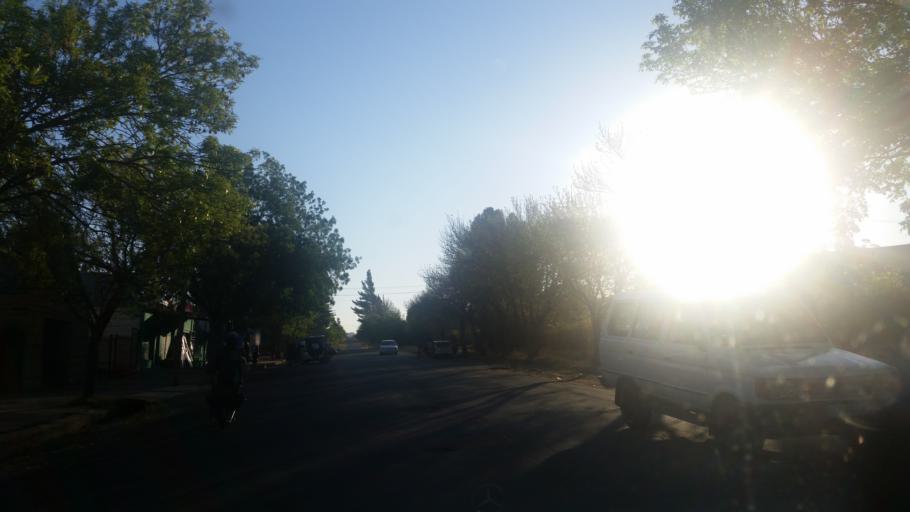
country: ZA
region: Orange Free State
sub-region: Thabo Mofutsanyana District Municipality
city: Phuthaditjhaba
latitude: -28.3140
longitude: 28.7029
